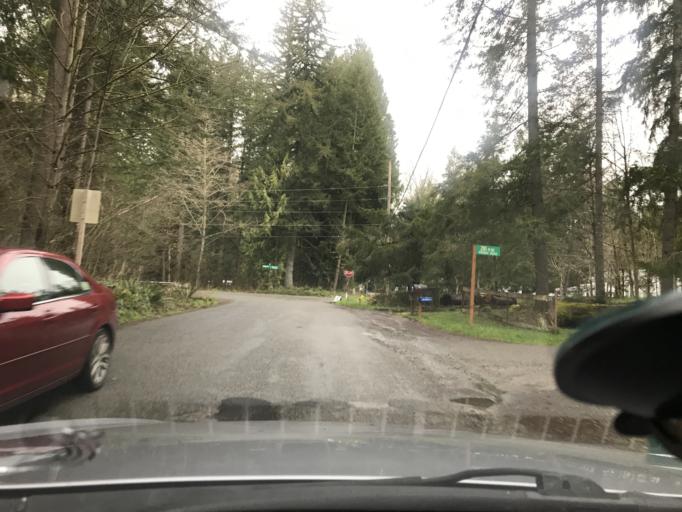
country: US
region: Washington
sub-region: King County
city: Ames Lake
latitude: 47.6441
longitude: -121.9628
